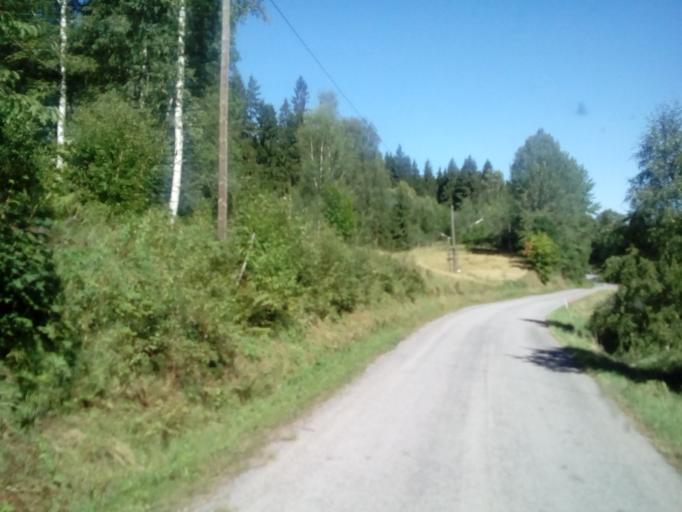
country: SE
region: Kalmar
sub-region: Vasterviks Kommun
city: Overum
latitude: 57.8713
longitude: 16.1196
